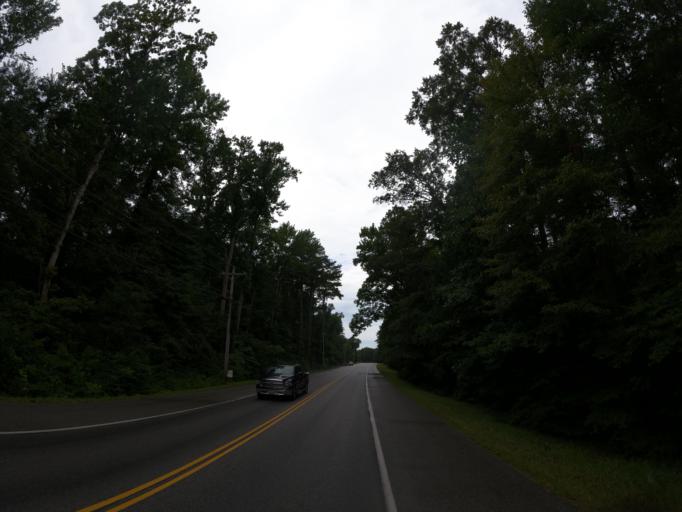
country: US
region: Maryland
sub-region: Saint Mary's County
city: California
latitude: 38.2599
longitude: -76.5215
